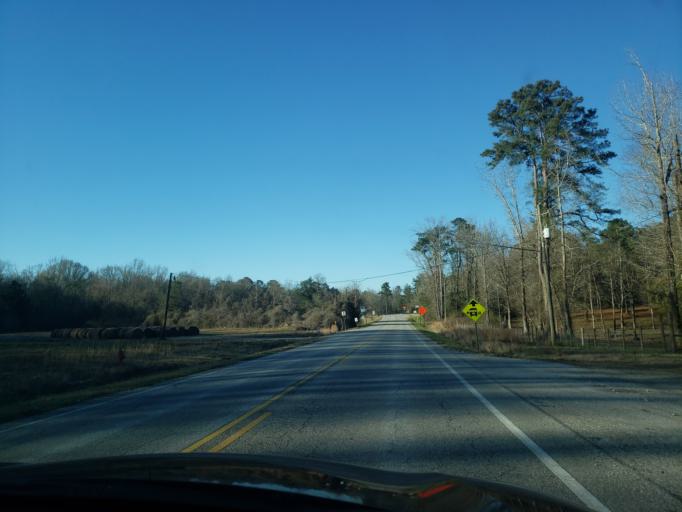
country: US
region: Alabama
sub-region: Macon County
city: Tuskegee
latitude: 32.5729
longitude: -85.6594
